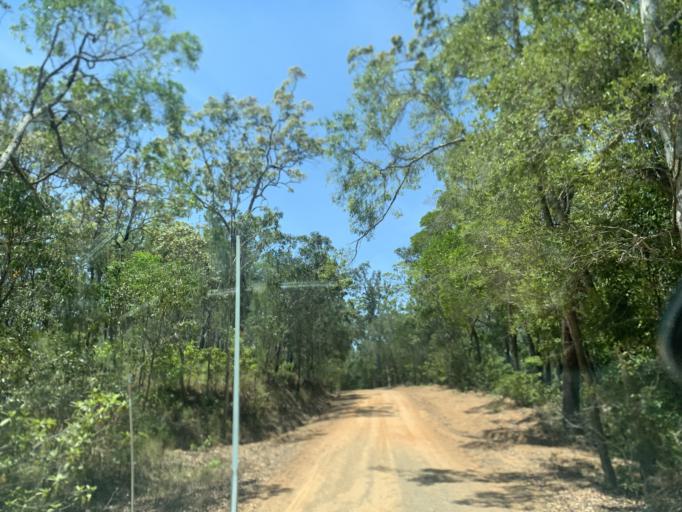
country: AU
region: Queensland
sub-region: Cairns
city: Redlynch
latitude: -16.9291
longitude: 145.6023
